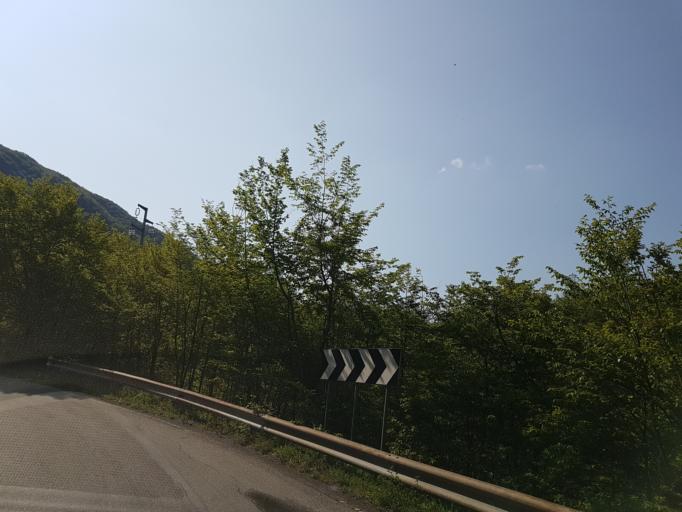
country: IT
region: Emilia-Romagna
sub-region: Forli-Cesena
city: San Piero in Bagno
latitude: 43.8112
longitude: 11.9249
